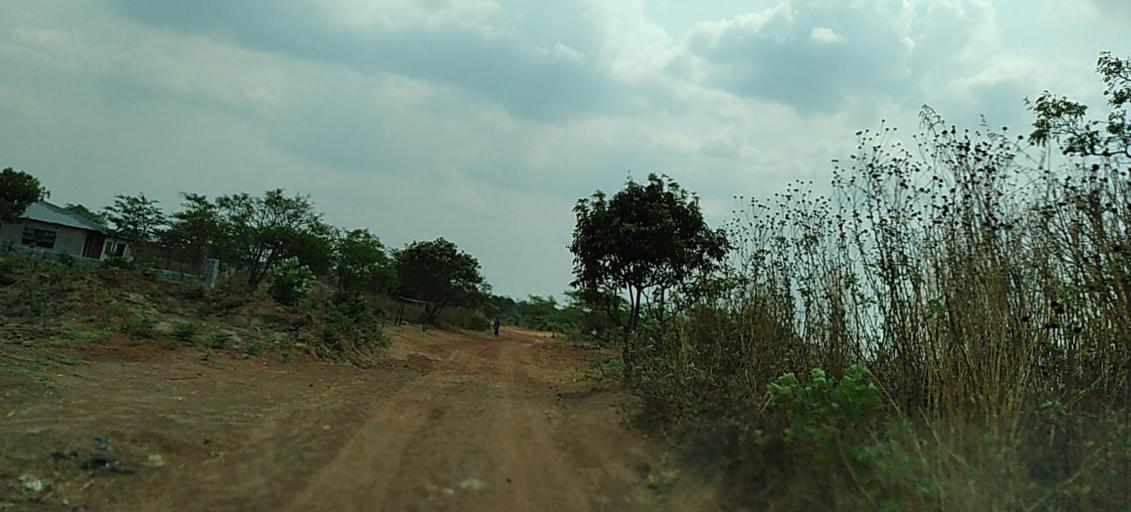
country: ZM
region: Copperbelt
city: Kalulushi
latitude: -12.8743
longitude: 28.0765
